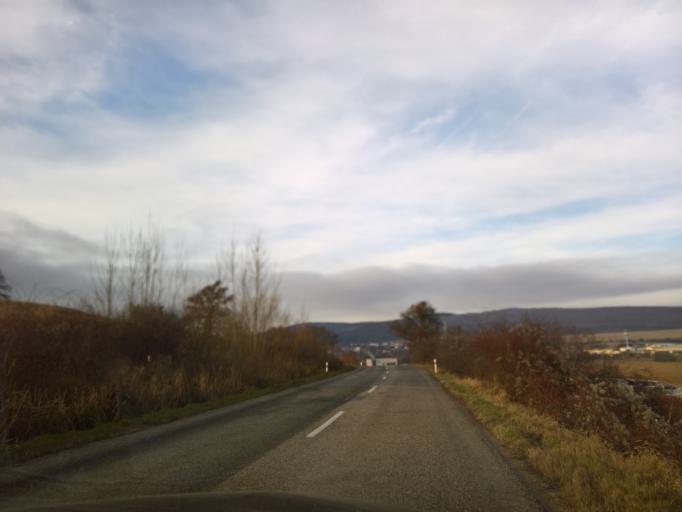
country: SK
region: Nitriansky
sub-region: Okres Nitra
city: Nitra
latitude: 48.3694
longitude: 18.1834
